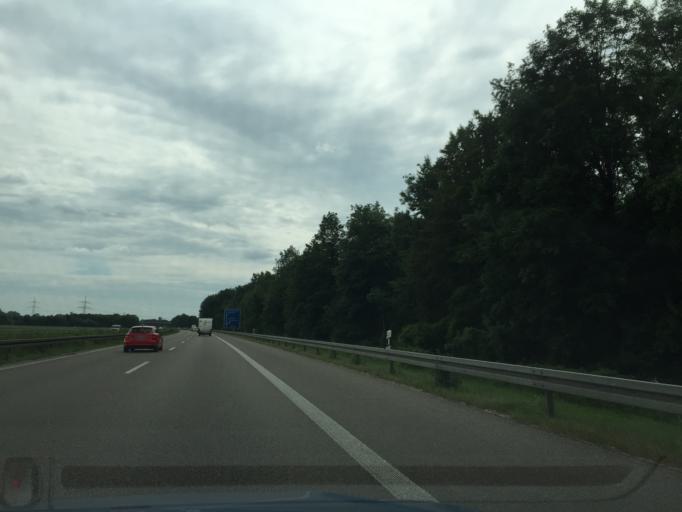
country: DE
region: Bavaria
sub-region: Swabia
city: Senden
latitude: 48.3437
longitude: 10.0229
